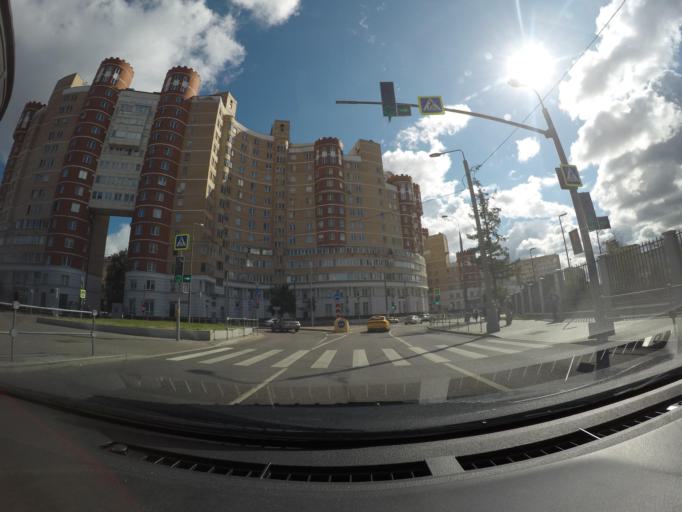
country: RU
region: Moskovskaya
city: Dorogomilovo
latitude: 55.7930
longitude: 37.5603
